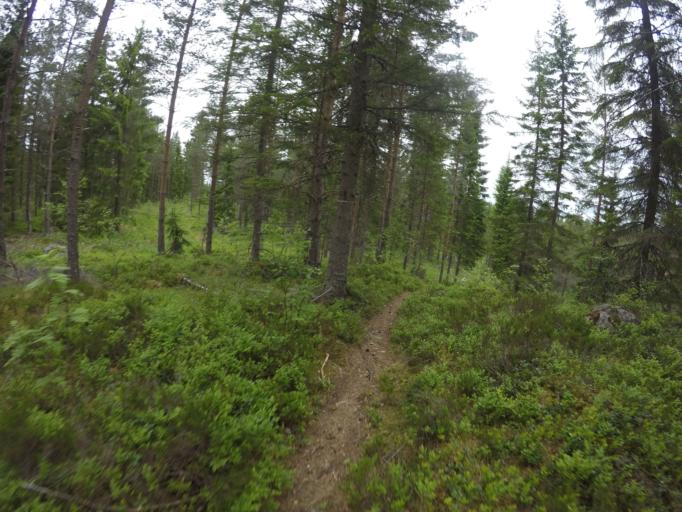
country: SE
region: Dalarna
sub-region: Ludvika Kommun
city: Abborrberget
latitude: 60.0773
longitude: 14.5240
